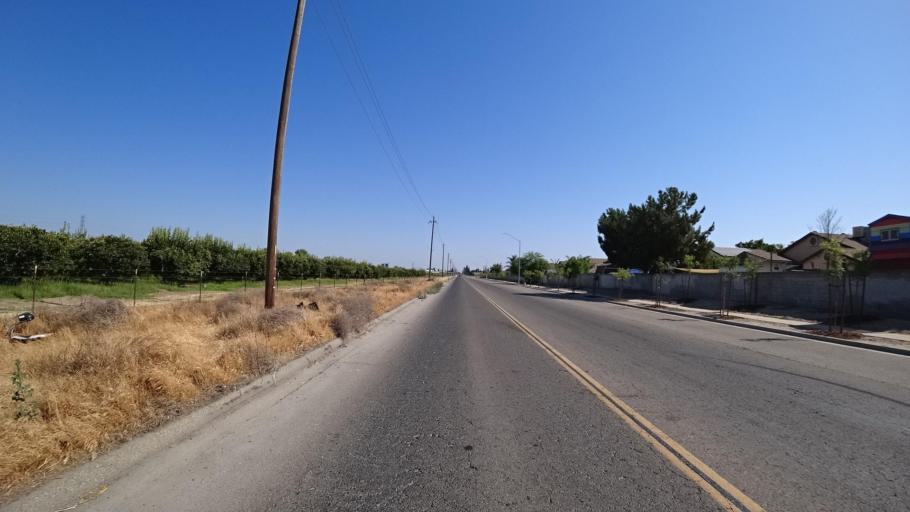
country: US
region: California
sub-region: Fresno County
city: West Park
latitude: 36.7079
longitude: -119.8180
